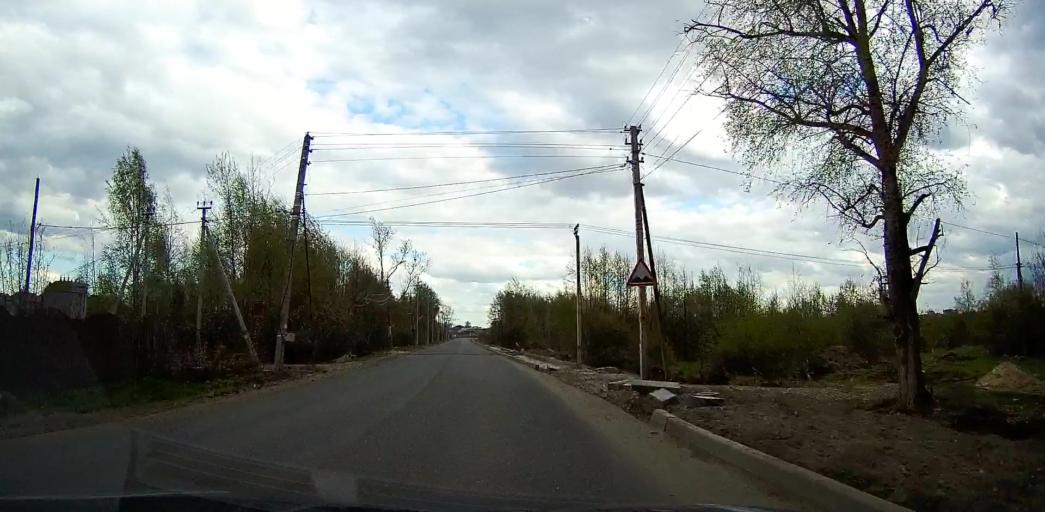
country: RU
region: Moskovskaya
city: Pavlovskiy Posad
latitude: 55.7996
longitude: 38.6862
